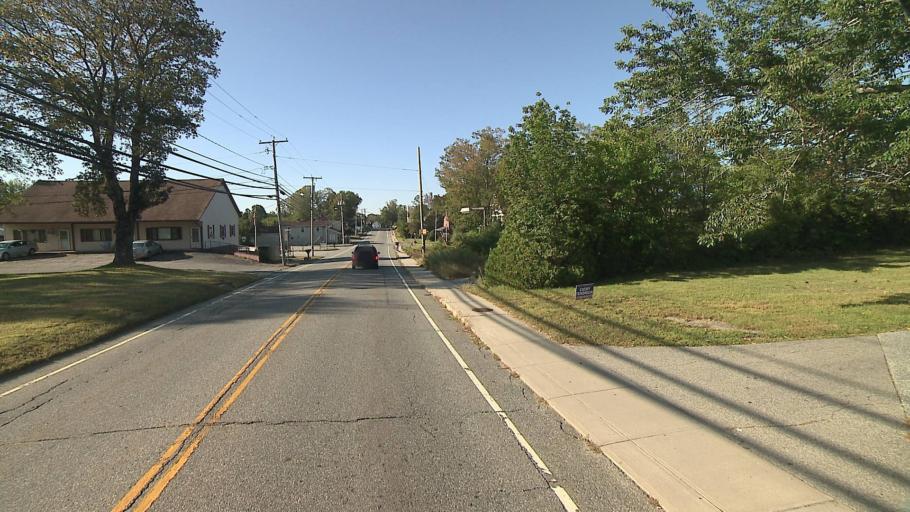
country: US
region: Connecticut
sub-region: Windham County
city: Plainfield
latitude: 41.6791
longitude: -71.9148
